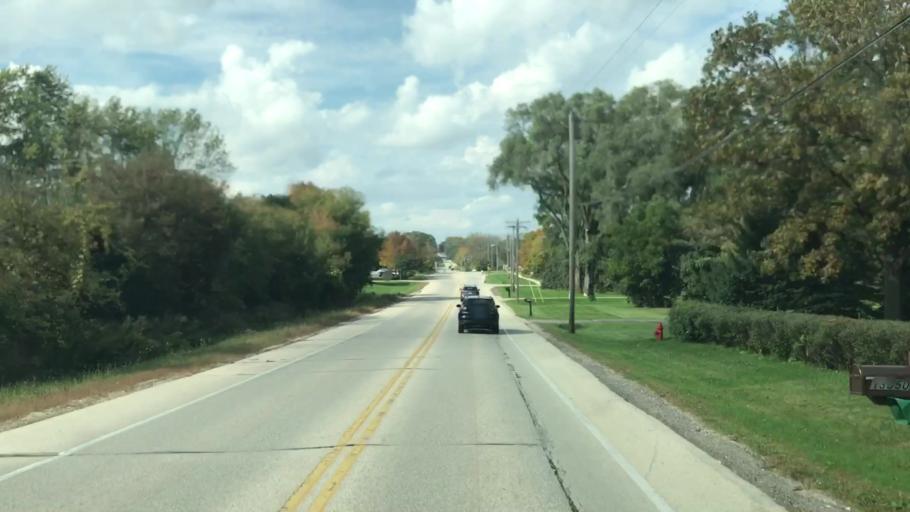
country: US
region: Wisconsin
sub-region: Waukesha County
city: Elm Grove
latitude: 43.0604
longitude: -88.0815
